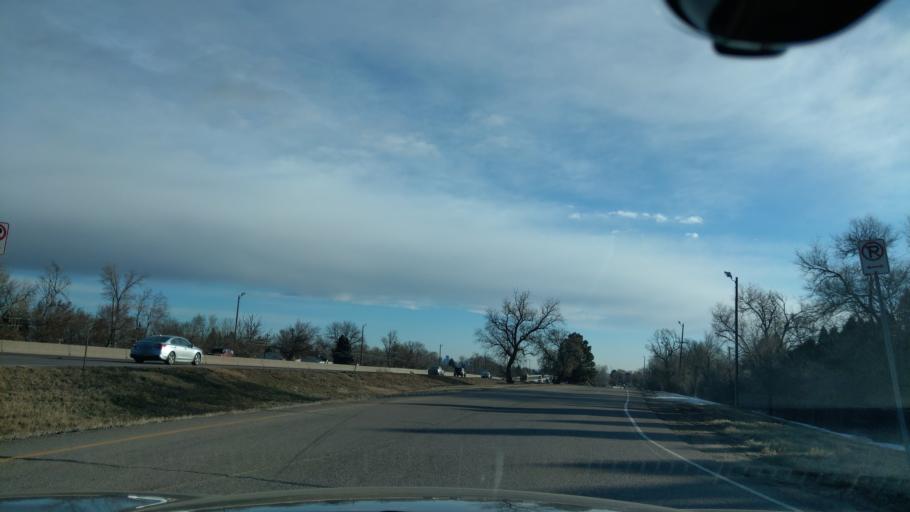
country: US
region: Colorado
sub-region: Jefferson County
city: Lakewood
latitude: 39.7251
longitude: -105.1069
